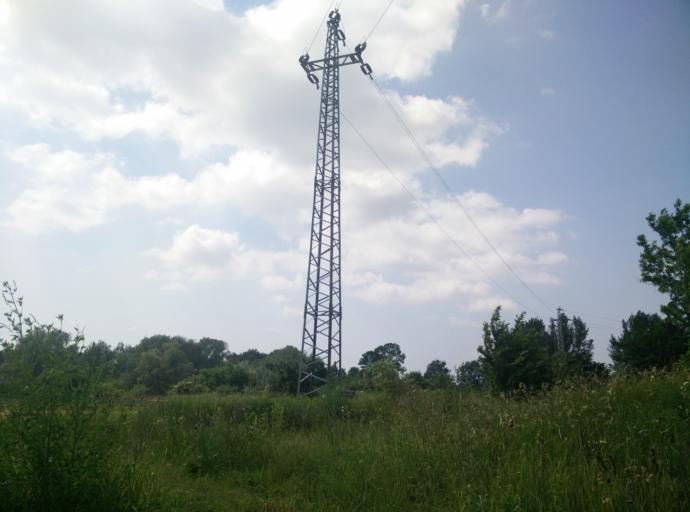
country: HU
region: Pest
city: Biatorbagy
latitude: 47.4568
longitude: 18.8121
